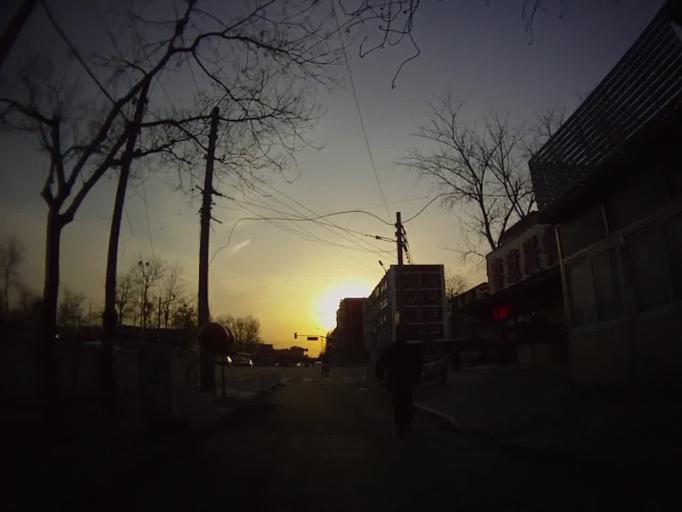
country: CN
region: Beijing
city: Longtan
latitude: 39.8800
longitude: 116.4285
